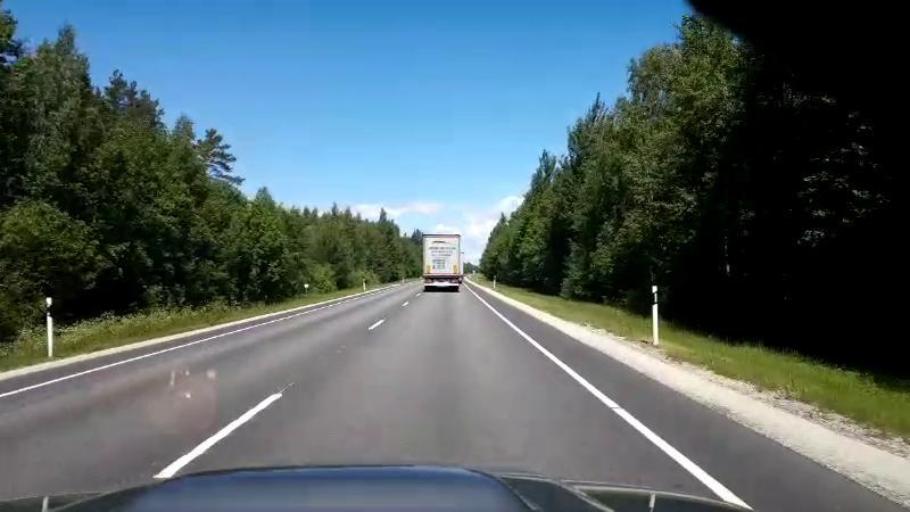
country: EE
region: Paernumaa
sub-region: Paernu linn
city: Parnu
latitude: 58.1047
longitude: 24.5084
